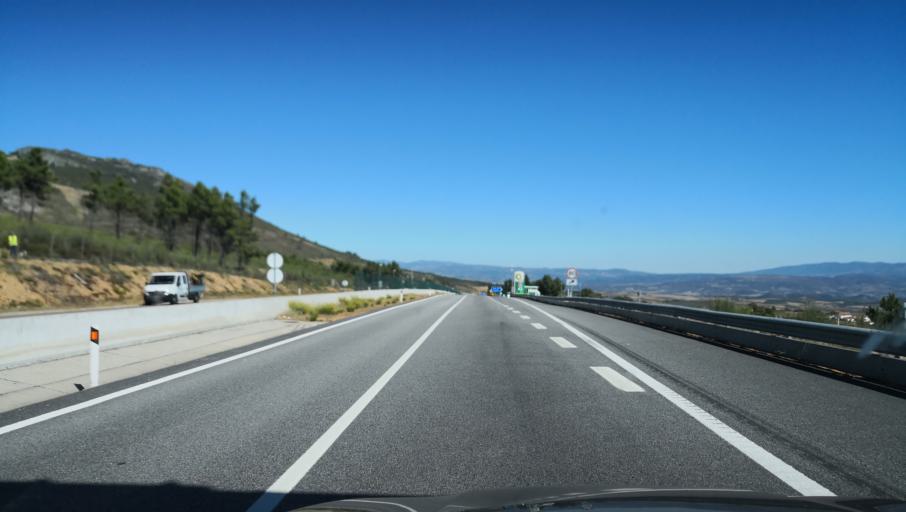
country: PT
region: Braganca
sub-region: Mirandela
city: Mirandela
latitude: 41.4408
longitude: -7.3065
